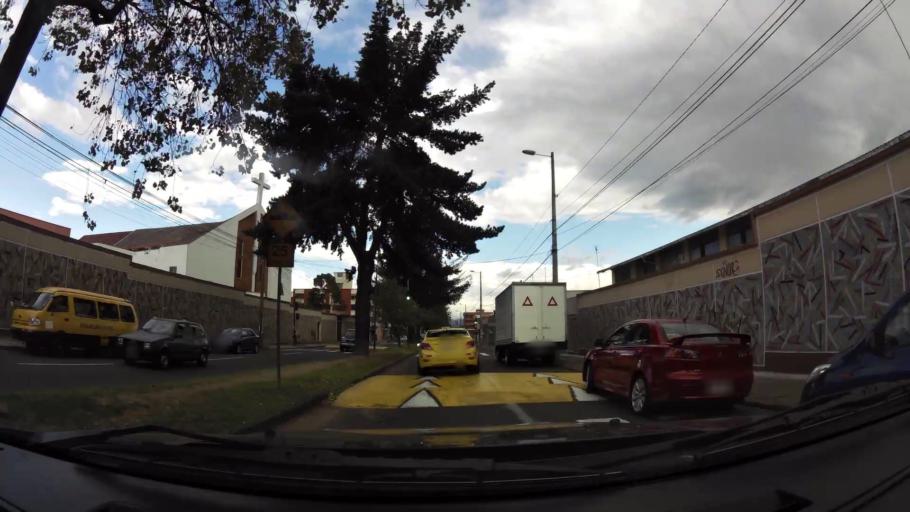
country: EC
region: Pichincha
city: Quito
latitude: -0.1321
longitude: -78.4871
